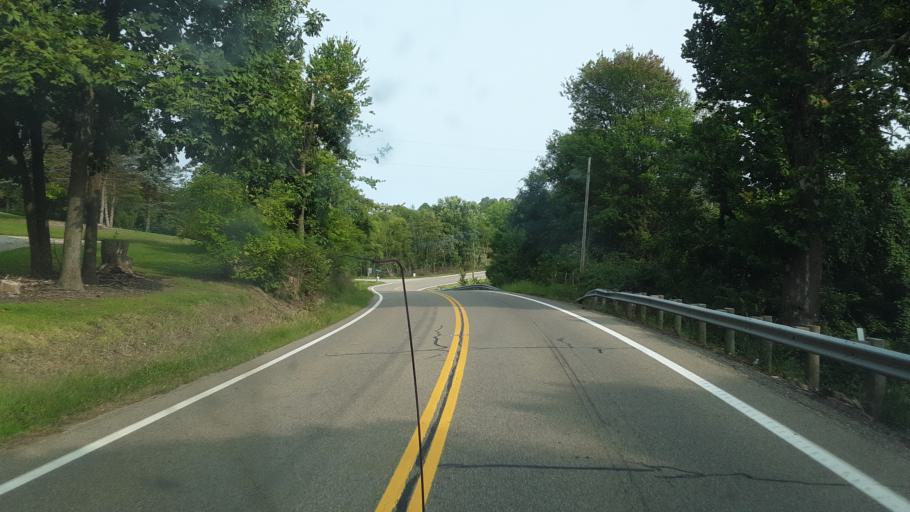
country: US
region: Ohio
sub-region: Coshocton County
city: Coshocton
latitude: 40.4131
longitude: -81.8845
